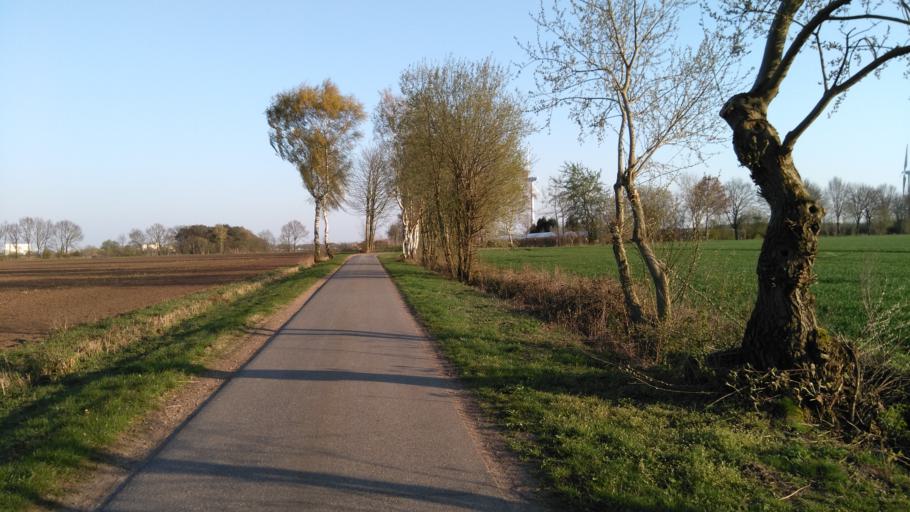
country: DE
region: Lower Saxony
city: Nottensdorf
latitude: 53.4570
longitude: 9.5948
